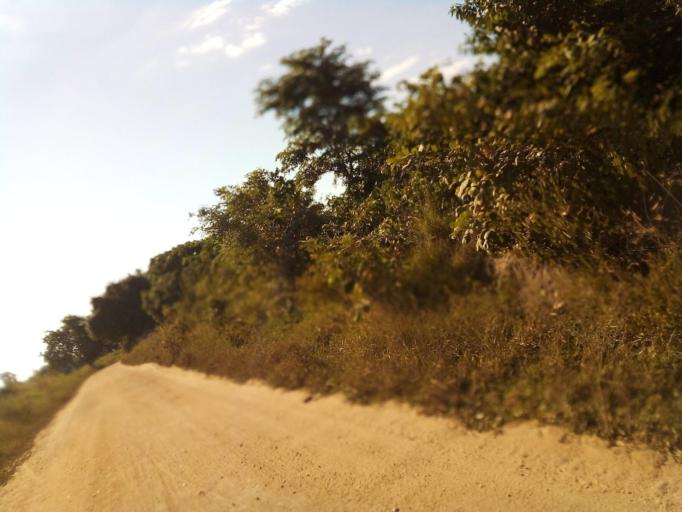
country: MZ
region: Zambezia
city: Quelimane
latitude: -17.5417
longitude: 36.6257
